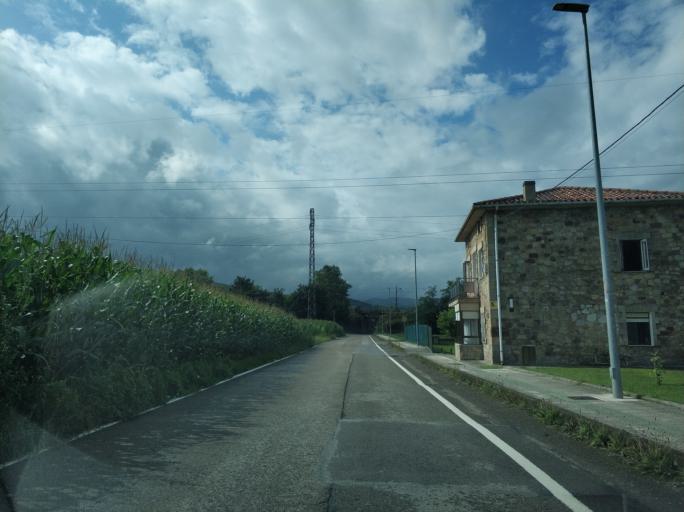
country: ES
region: Cantabria
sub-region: Provincia de Cantabria
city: Polanco
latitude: 43.3619
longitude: -3.9642
